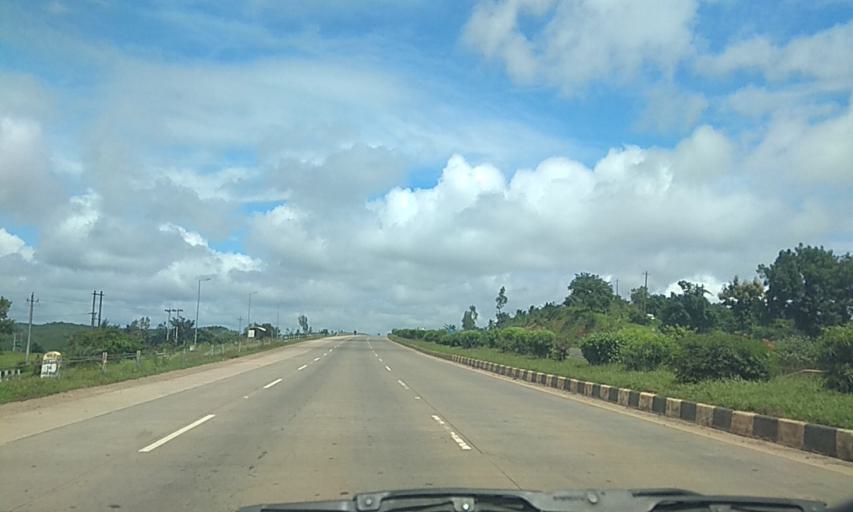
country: IN
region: Karnataka
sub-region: Dharwad
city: Alnavar
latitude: 15.6129
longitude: 74.7647
